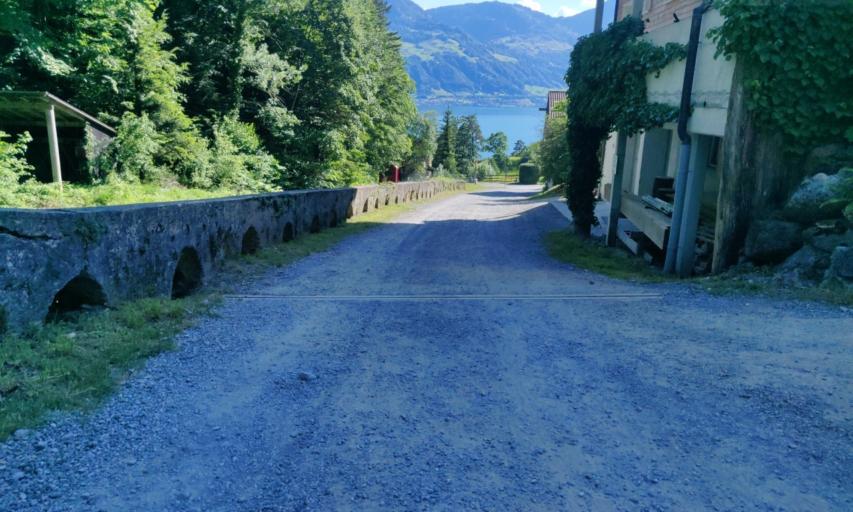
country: CH
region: Schwyz
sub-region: Bezirk Gersau
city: Gersau
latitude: 46.9968
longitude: 8.5286
